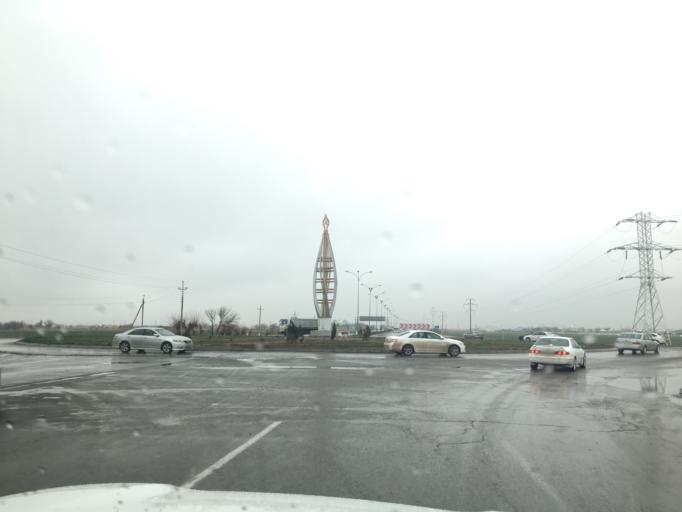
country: TM
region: Mary
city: Mary
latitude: 37.5832
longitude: 61.7891
